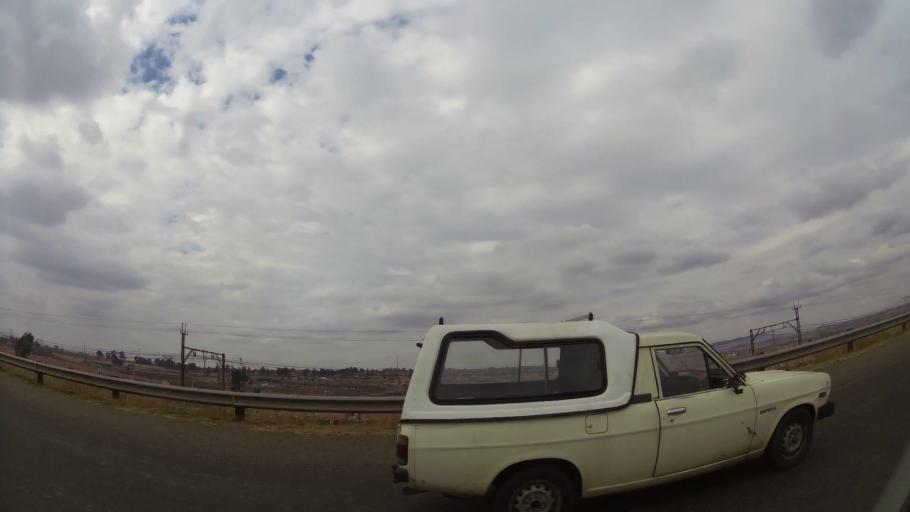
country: ZA
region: Gauteng
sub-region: Ekurhuleni Metropolitan Municipality
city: Germiston
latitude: -26.3713
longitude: 28.1121
